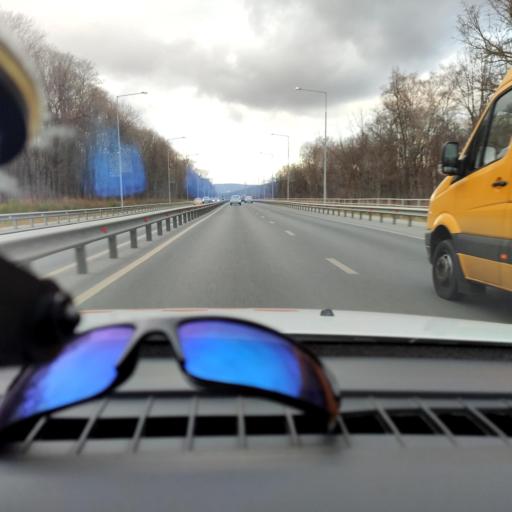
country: RU
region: Samara
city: Volzhskiy
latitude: 53.3595
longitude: 50.2059
